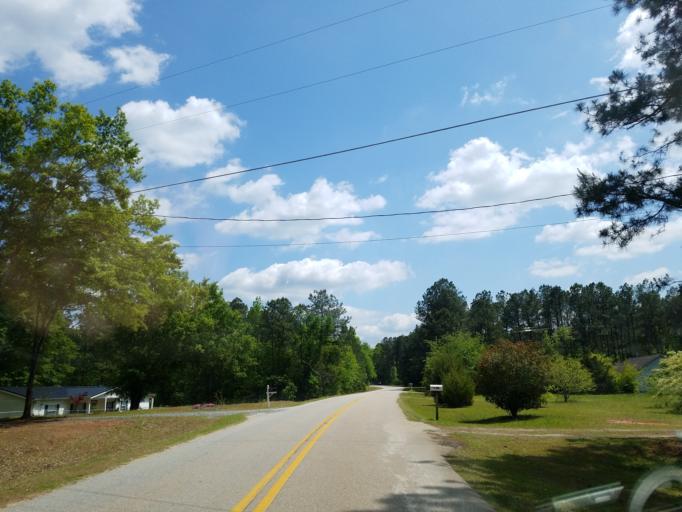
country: US
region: Georgia
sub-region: Monroe County
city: Forsyth
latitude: 33.0907
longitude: -83.9613
